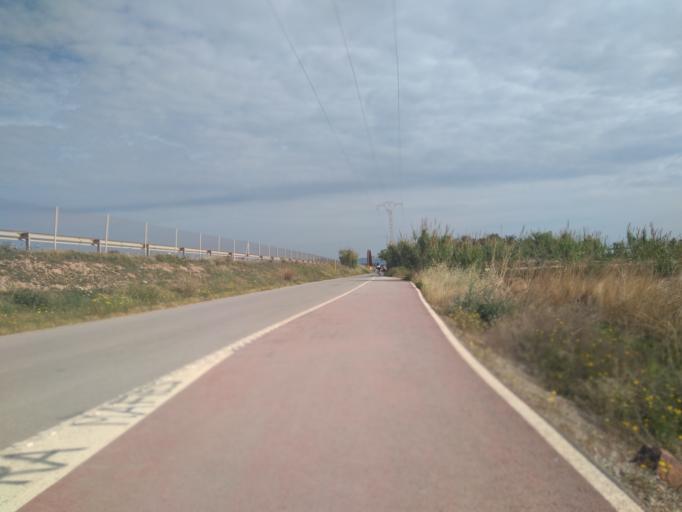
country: ES
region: Valencia
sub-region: Provincia de Valencia
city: Alboraya
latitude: 39.4993
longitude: -0.3253
